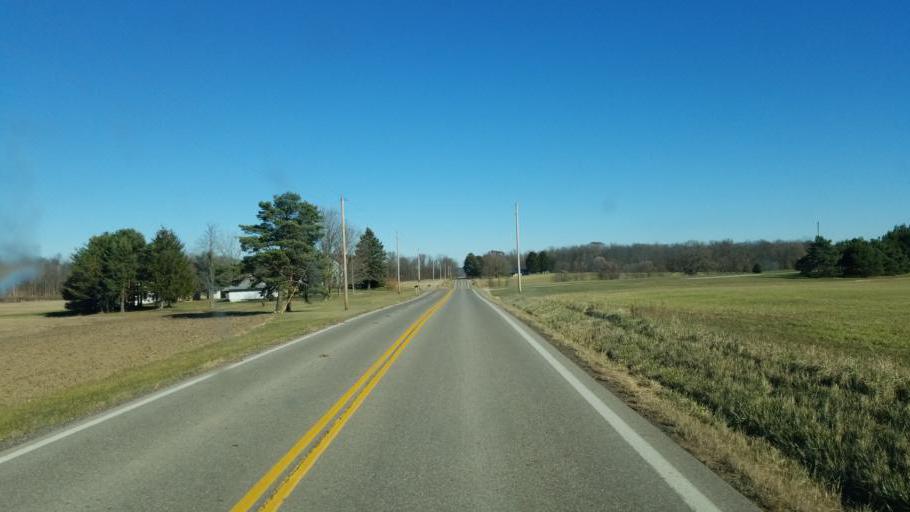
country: US
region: Ohio
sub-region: Ashland County
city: Ashland
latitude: 40.9405
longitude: -82.3874
